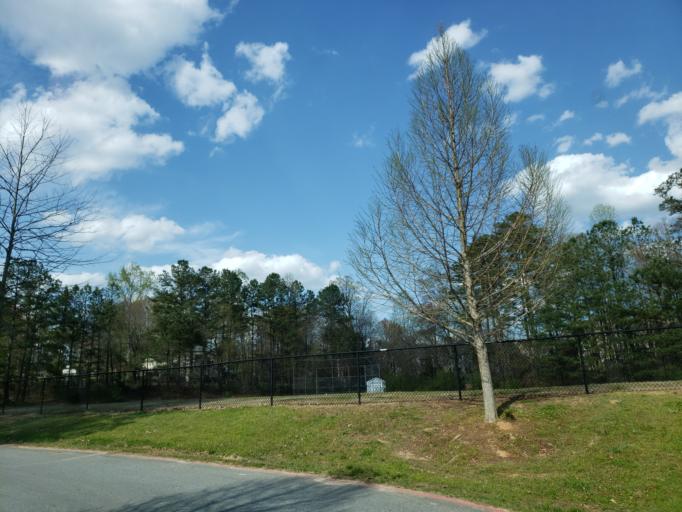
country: US
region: Georgia
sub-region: Cherokee County
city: Woodstock
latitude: 34.0336
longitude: -84.4773
